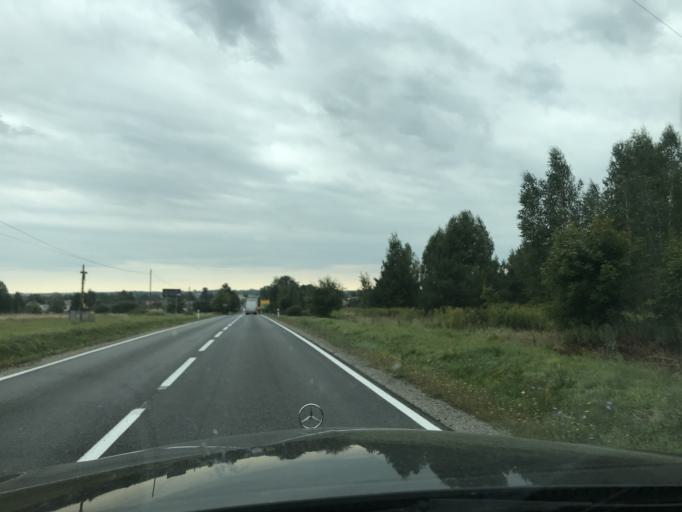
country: PL
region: Subcarpathian Voivodeship
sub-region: Powiat nizanski
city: Jezowe
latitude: 50.3798
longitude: 22.1283
